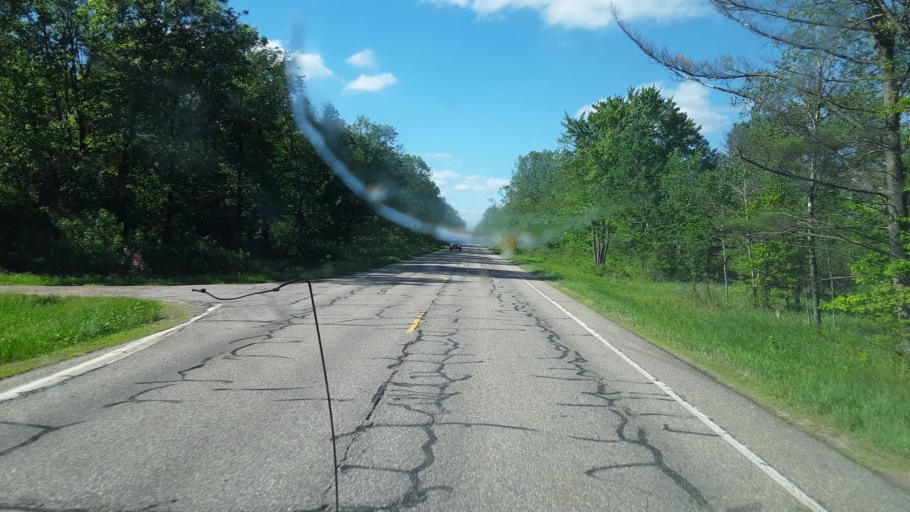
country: US
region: Wisconsin
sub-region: Wood County
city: Nekoosa
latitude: 44.2526
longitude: -90.1402
